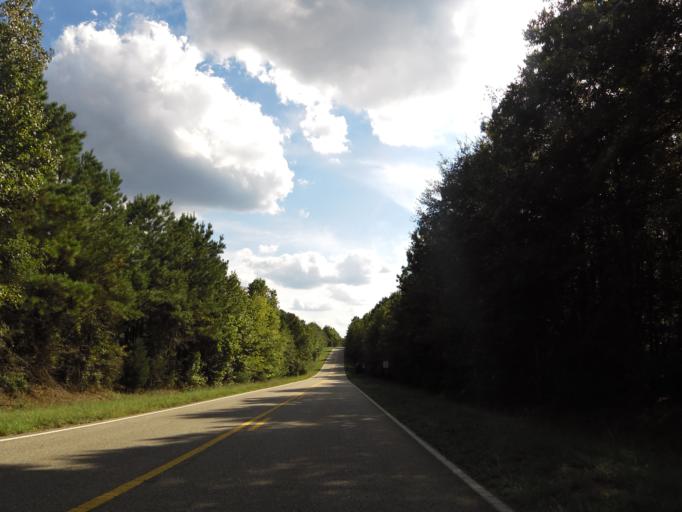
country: US
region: Alabama
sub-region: Dallas County
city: Selmont-West Selmont
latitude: 32.1498
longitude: -87.0734
